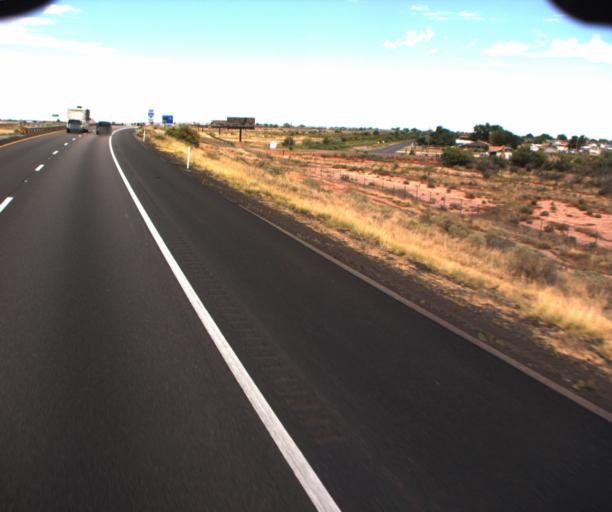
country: US
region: Arizona
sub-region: Navajo County
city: Winslow
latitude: 35.0227
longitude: -110.6804
